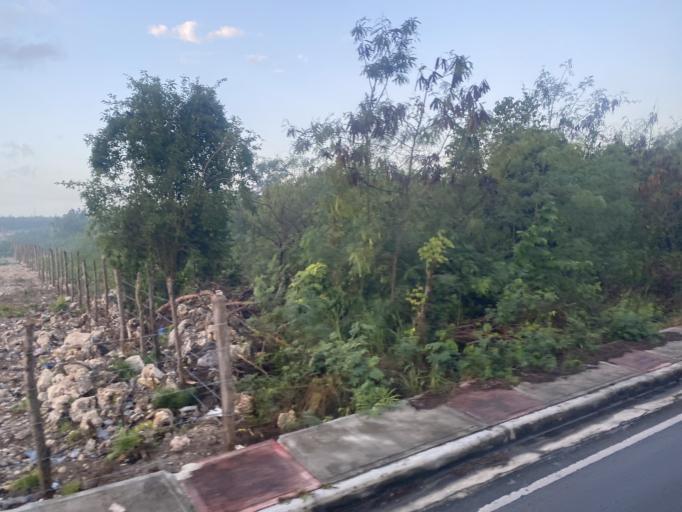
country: DO
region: San Juan
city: Punta Cana
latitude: 18.7113
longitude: -68.4643
